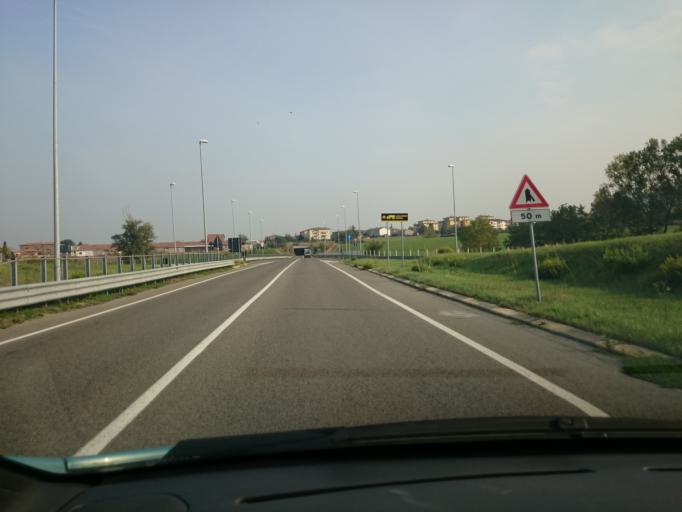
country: IT
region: Emilia-Romagna
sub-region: Provincia di Reggio Emilia
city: Casalgrande
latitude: 44.5854
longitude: 10.7264
